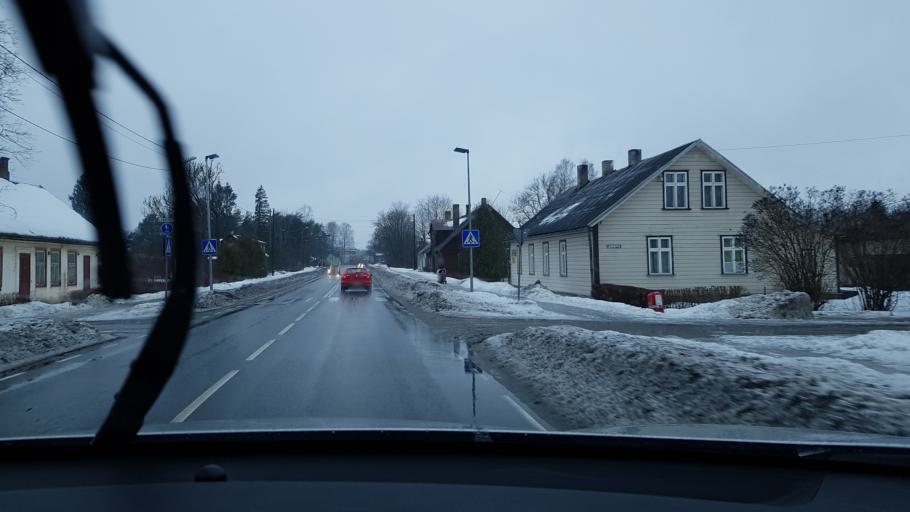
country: EE
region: Jaervamaa
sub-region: Tueri vald
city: Tueri
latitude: 58.8087
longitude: 25.4226
